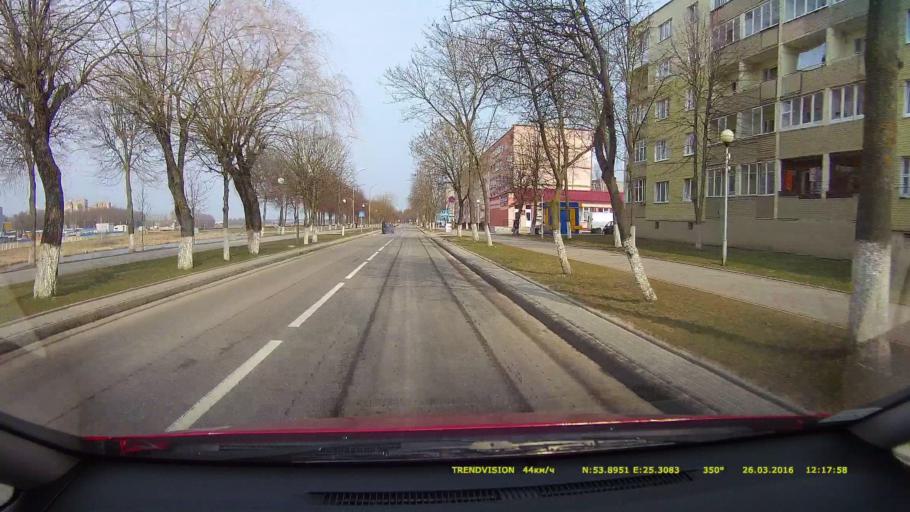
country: BY
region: Grodnenskaya
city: Lida
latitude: 53.8952
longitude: 25.3083
